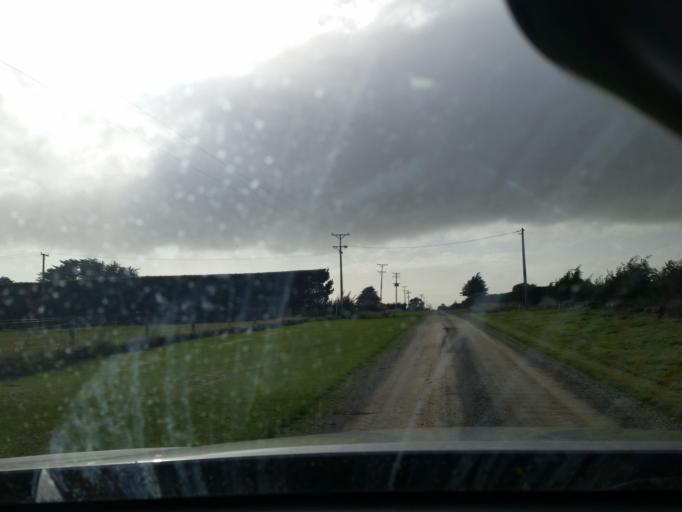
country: NZ
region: Southland
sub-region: Invercargill City
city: Invercargill
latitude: -46.3320
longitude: 168.3661
